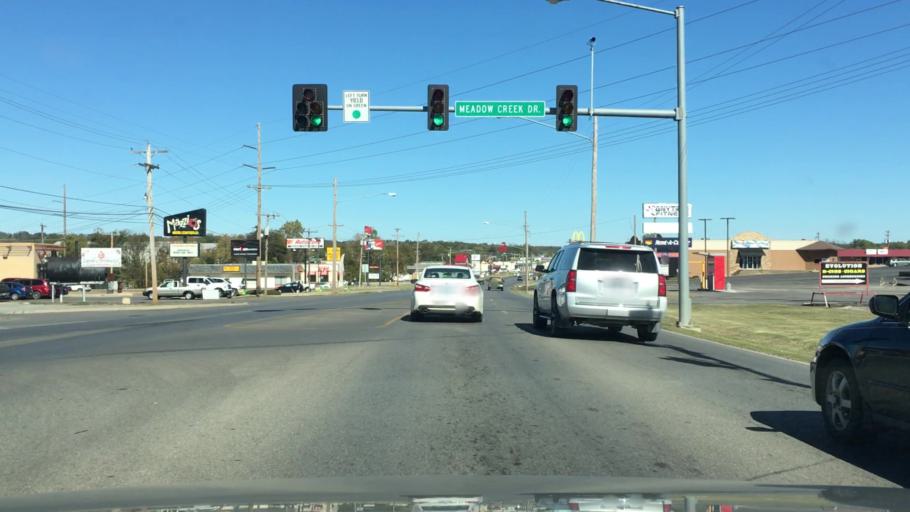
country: US
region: Oklahoma
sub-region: Cherokee County
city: Tahlequah
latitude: 35.8931
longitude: -94.9772
